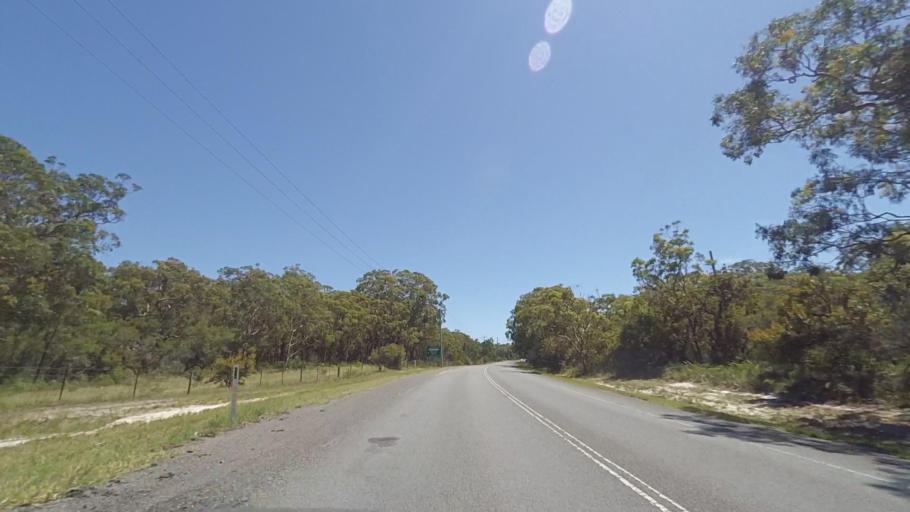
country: AU
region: New South Wales
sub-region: Port Stephens Shire
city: Medowie
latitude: -32.7759
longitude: 151.8587
